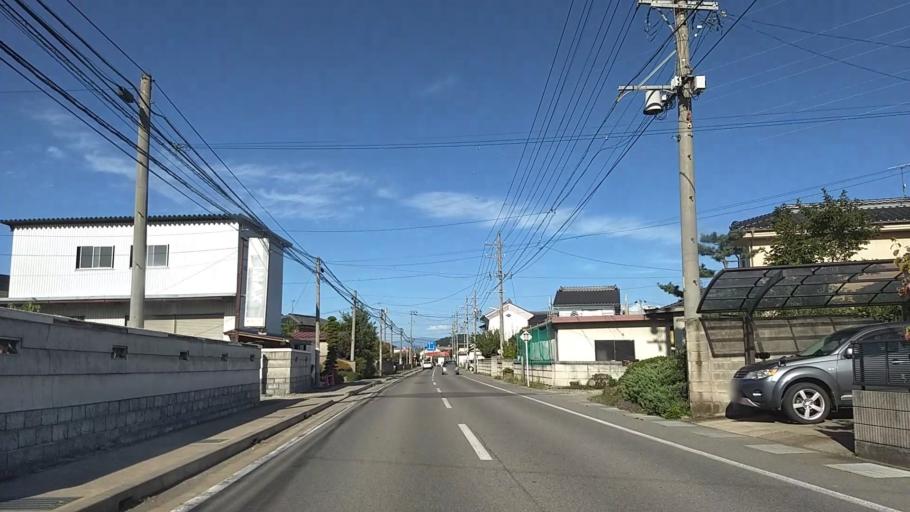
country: JP
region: Nagano
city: Nagano-shi
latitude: 36.5447
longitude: 138.1350
